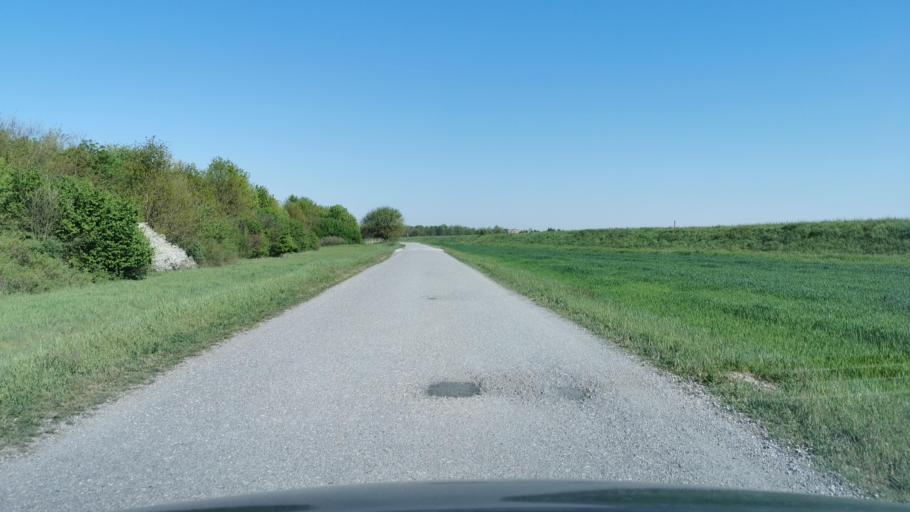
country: IT
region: Lombardy
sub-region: Provincia di Cremona
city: Bosco Ex Parmigiano
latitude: 45.1138
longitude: 10.0165
